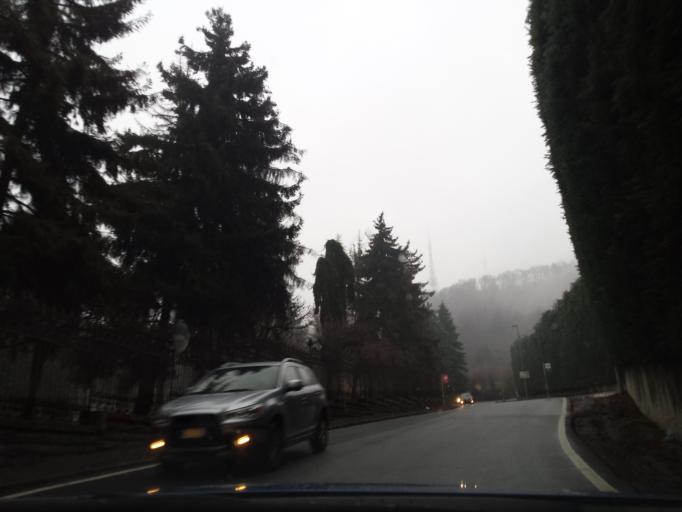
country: IT
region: Piedmont
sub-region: Provincia di Torino
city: Revigliasco
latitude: 45.0463
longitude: 7.7281
